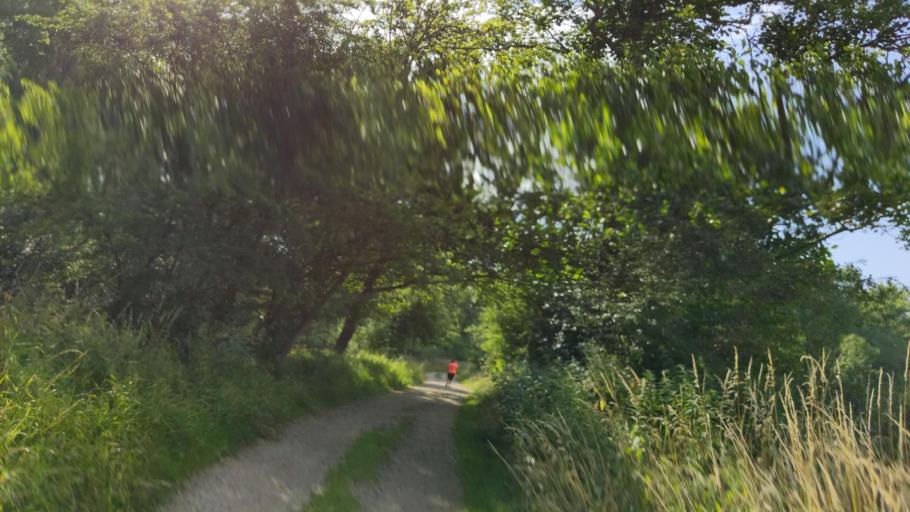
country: DE
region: Schleswig-Holstein
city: Travemuende
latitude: 53.9491
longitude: 10.8775
